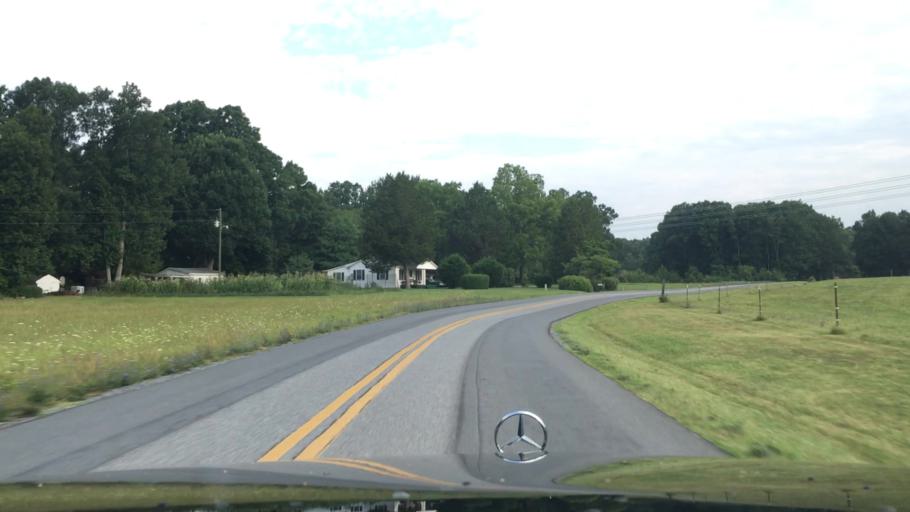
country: US
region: Virginia
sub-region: Campbell County
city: Timberlake
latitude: 37.2814
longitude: -79.3188
